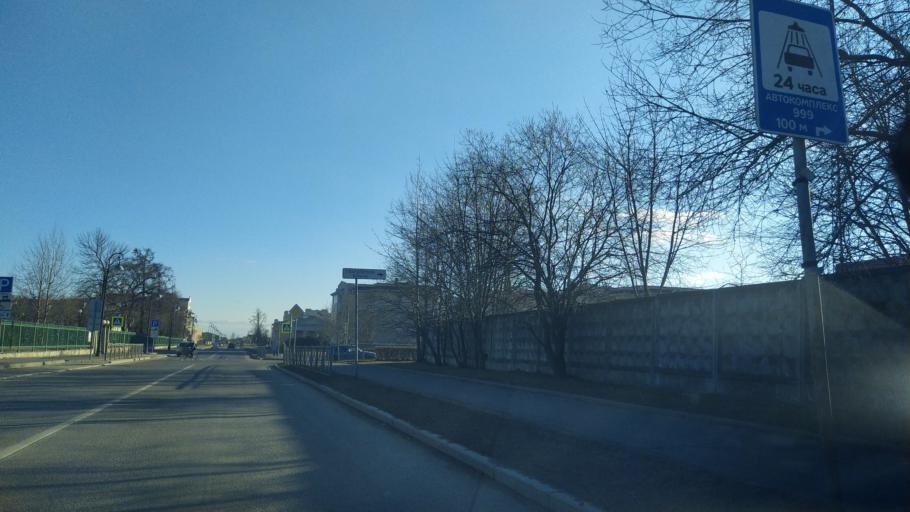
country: RU
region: St.-Petersburg
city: Pushkin
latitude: 59.7058
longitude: 30.3913
